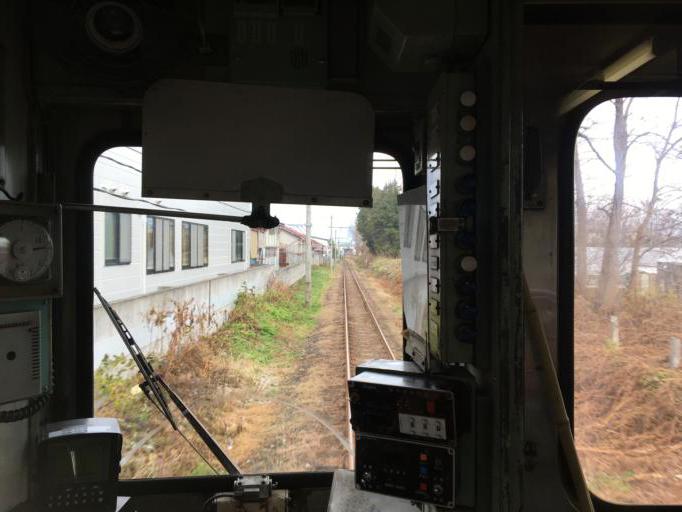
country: JP
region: Aomori
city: Hirosaki
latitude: 40.5777
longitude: 140.4725
